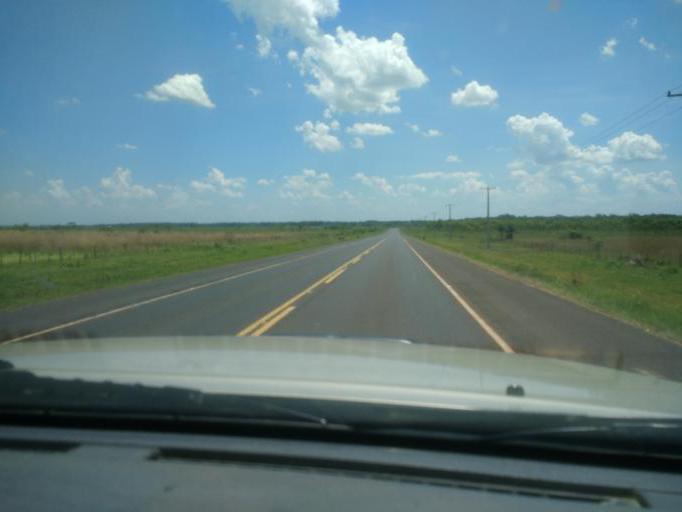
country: PY
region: San Pedro
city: Itacurubi del Rosario
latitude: -24.5243
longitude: -56.8257
